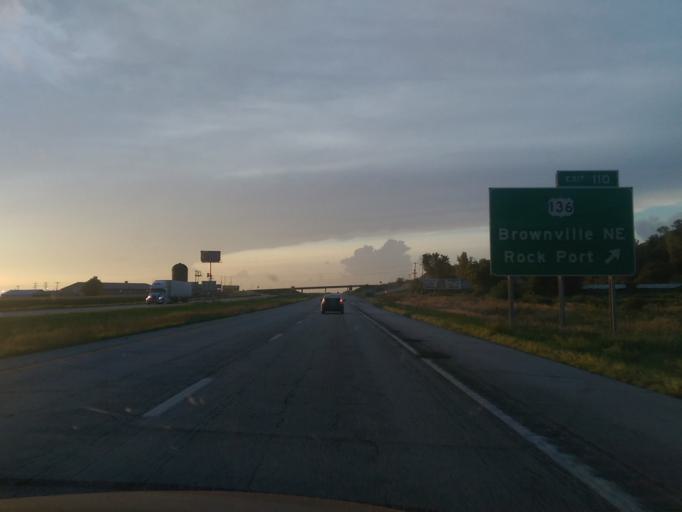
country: US
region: Missouri
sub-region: Atchison County
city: Rock Port
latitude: 40.4012
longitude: -95.5520
